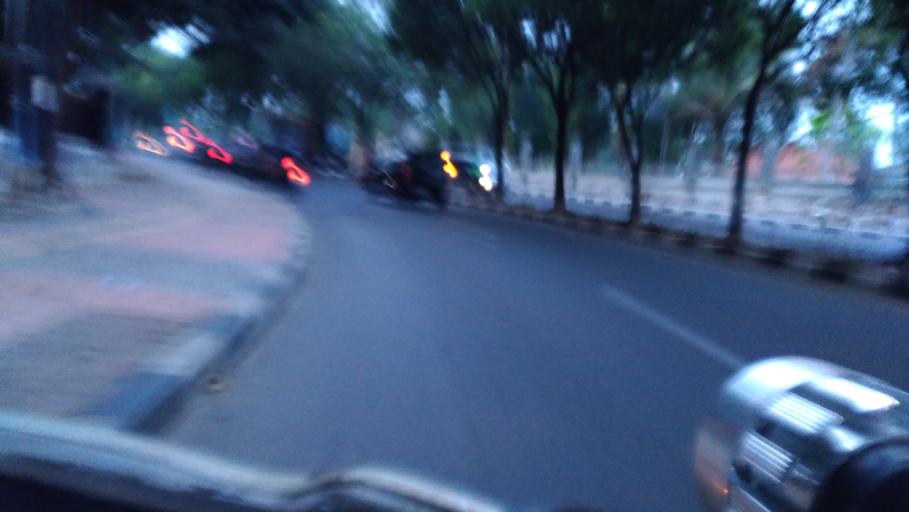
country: ID
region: West Java
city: Cileungsir
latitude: -6.3685
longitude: 106.8897
